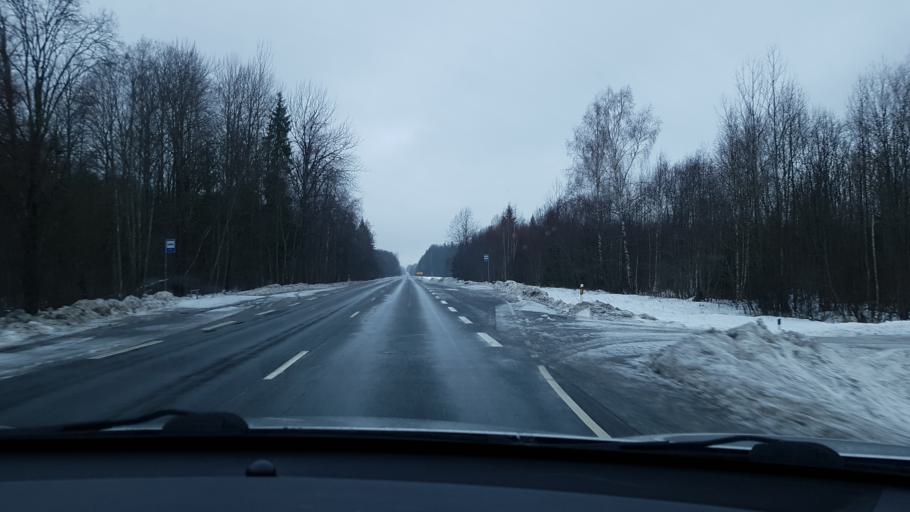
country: EE
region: Jaervamaa
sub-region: Tueri vald
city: Sarevere
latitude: 58.8050
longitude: 25.2162
